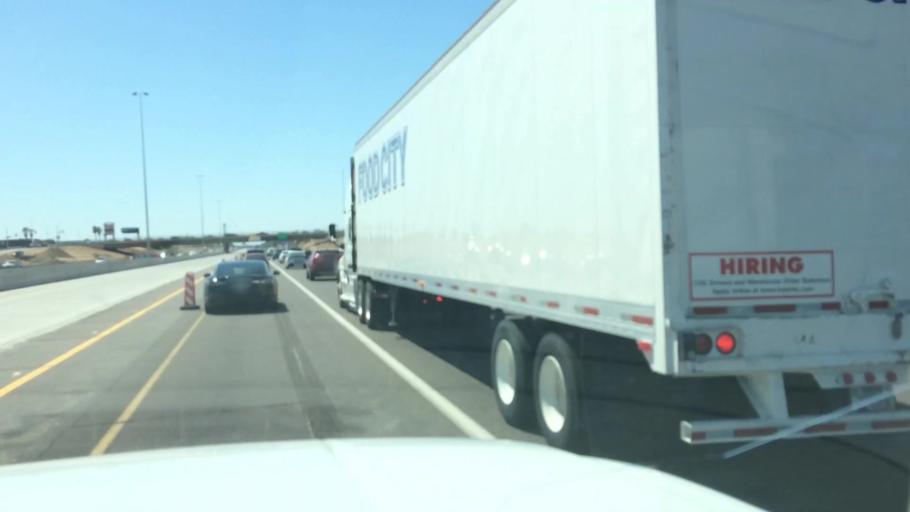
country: US
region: Arizona
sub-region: Maricopa County
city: Tolleson
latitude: 33.4617
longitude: -112.2009
